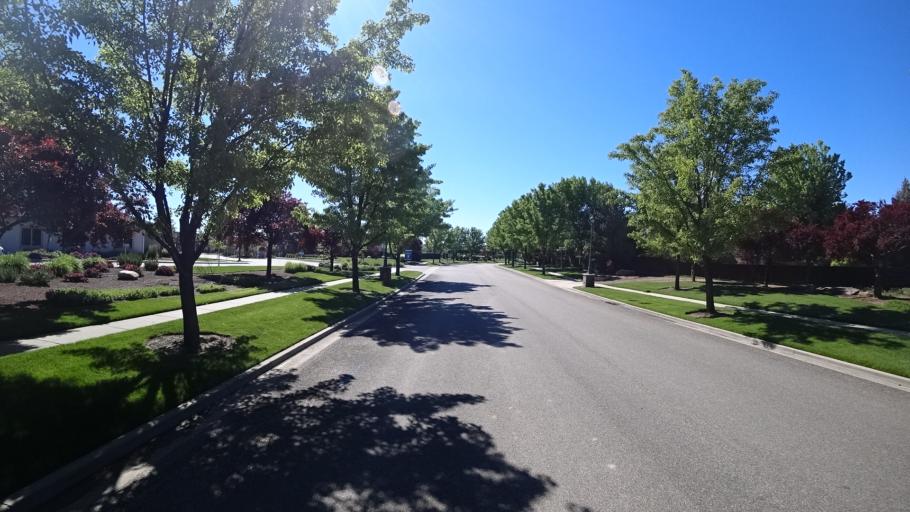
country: US
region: Idaho
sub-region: Ada County
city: Meridian
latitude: 43.6614
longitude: -116.4020
